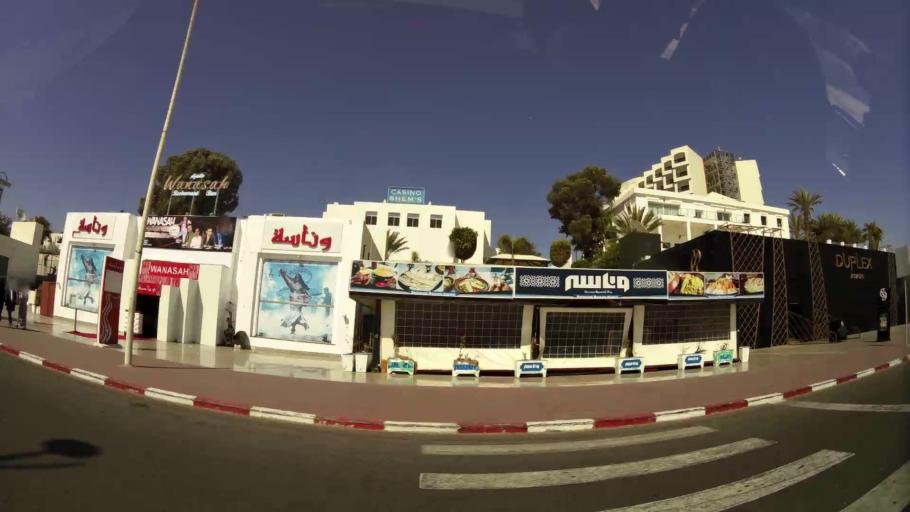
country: MA
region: Souss-Massa-Draa
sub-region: Agadir-Ida-ou-Tnan
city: Agadir
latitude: 30.4191
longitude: -9.6051
